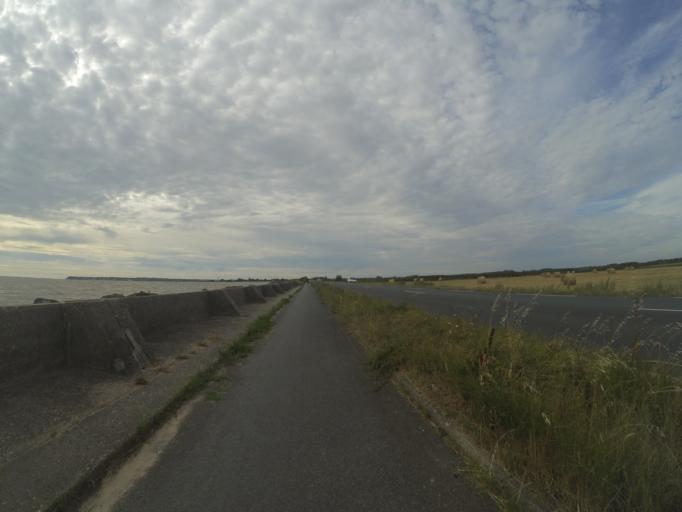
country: FR
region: Poitou-Charentes
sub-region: Departement de la Charente-Maritime
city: Meschers-sur-Gironde
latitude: 45.5440
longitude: -0.9101
